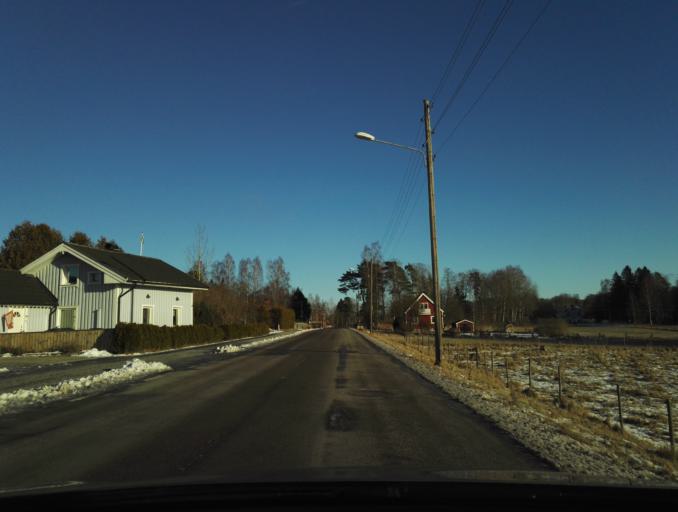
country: SE
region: Kronoberg
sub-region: Vaxjo Kommun
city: Gemla
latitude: 56.8617
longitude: 14.6326
